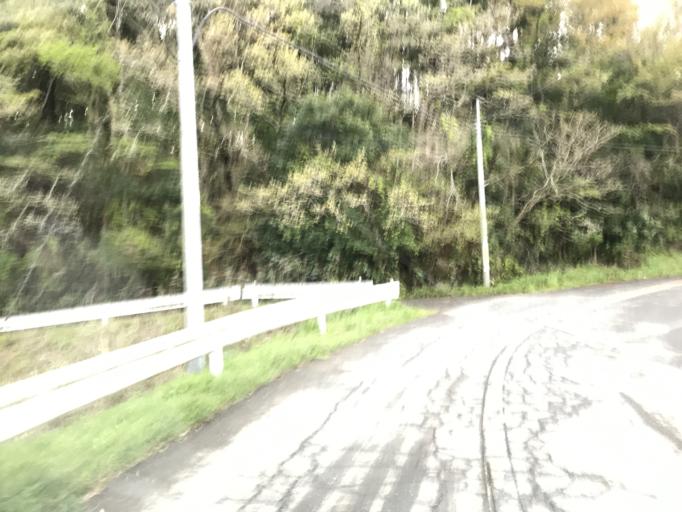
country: JP
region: Chiba
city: Sawara
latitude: 35.7752
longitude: 140.4527
